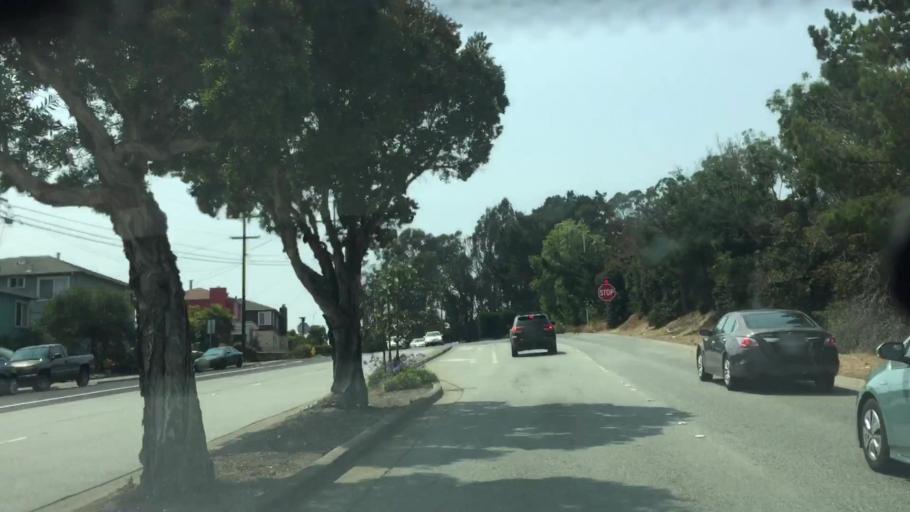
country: US
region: California
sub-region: San Mateo County
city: South San Francisco
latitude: 37.6687
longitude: -122.4234
